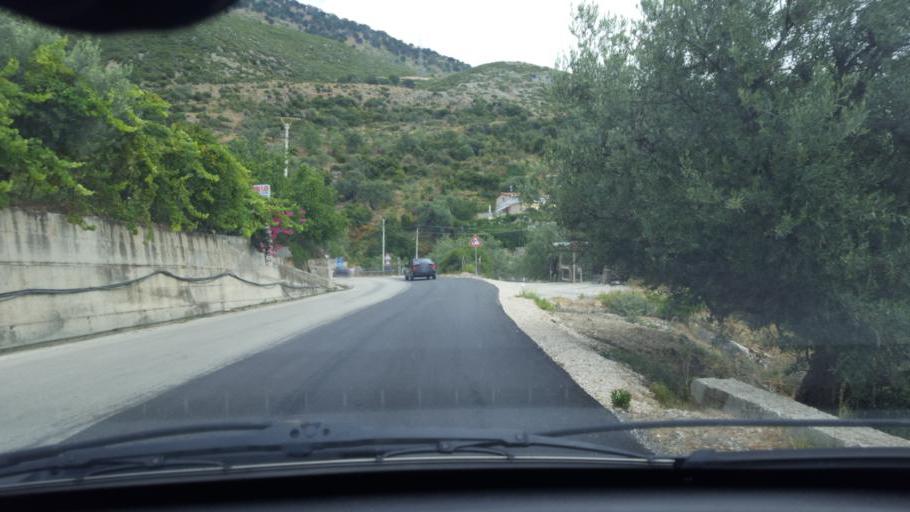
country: AL
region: Vlore
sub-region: Rrethi i Sarandes
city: Lukove
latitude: 40.0539
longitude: 19.8688
